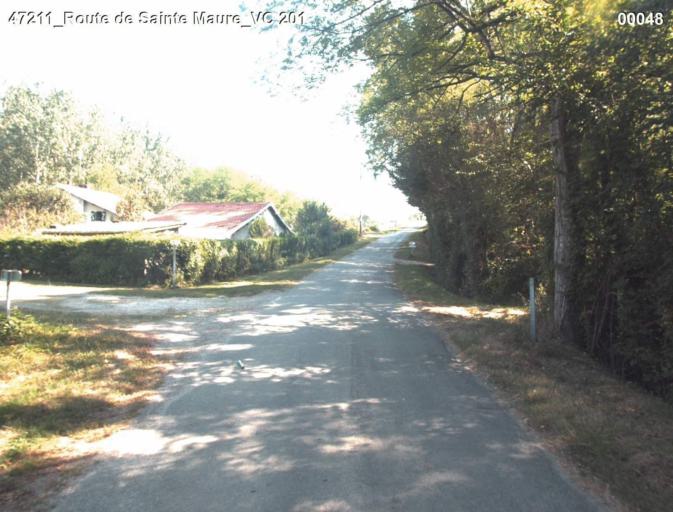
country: FR
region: Aquitaine
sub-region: Departement du Lot-et-Garonne
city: Mezin
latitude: 44.0390
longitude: 0.1953
